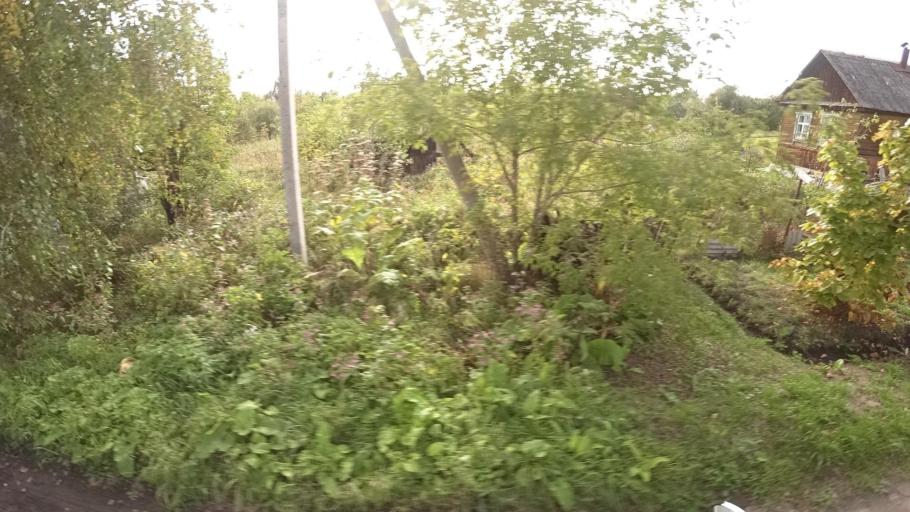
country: RU
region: Primorskiy
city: Dostoyevka
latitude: 44.2891
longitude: 133.4306
